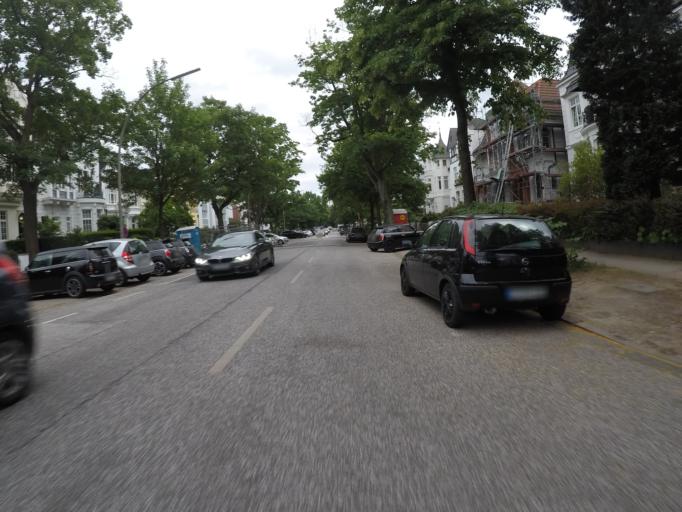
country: DE
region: Hamburg
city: Hamburg-Nord
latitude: 53.5869
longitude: 9.9951
